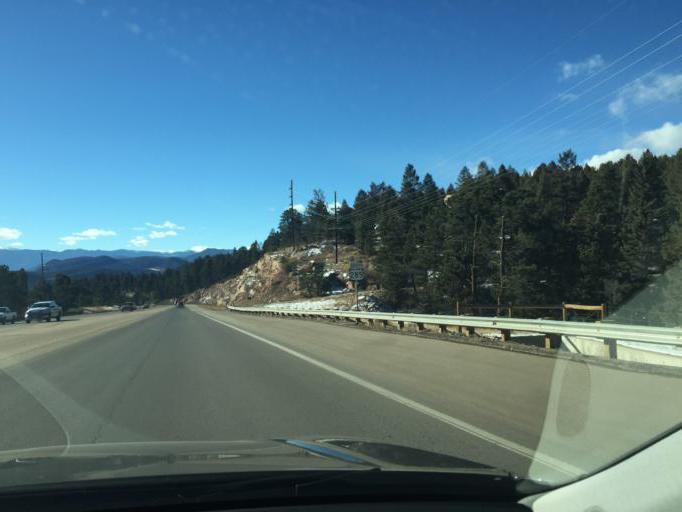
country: US
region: Colorado
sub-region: Jefferson County
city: Evergreen
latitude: 39.4960
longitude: -105.3369
